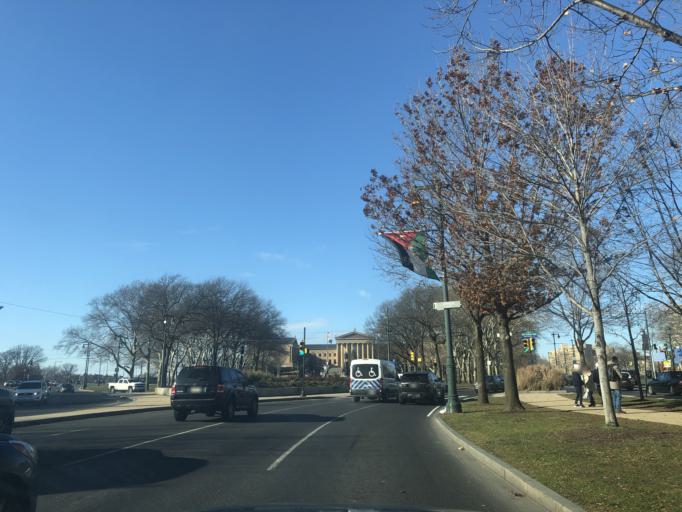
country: US
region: Pennsylvania
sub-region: Philadelphia County
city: Philadelphia
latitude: 39.9625
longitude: -75.1766
